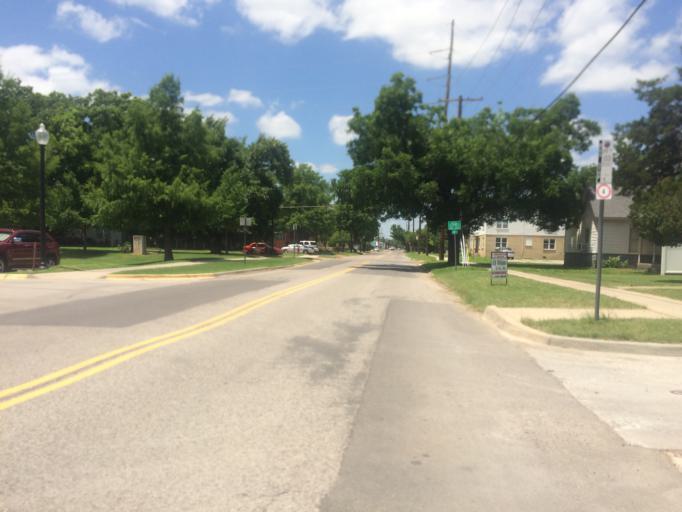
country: US
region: Oklahoma
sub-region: Cleveland County
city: Norman
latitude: 35.2162
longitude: -97.4446
